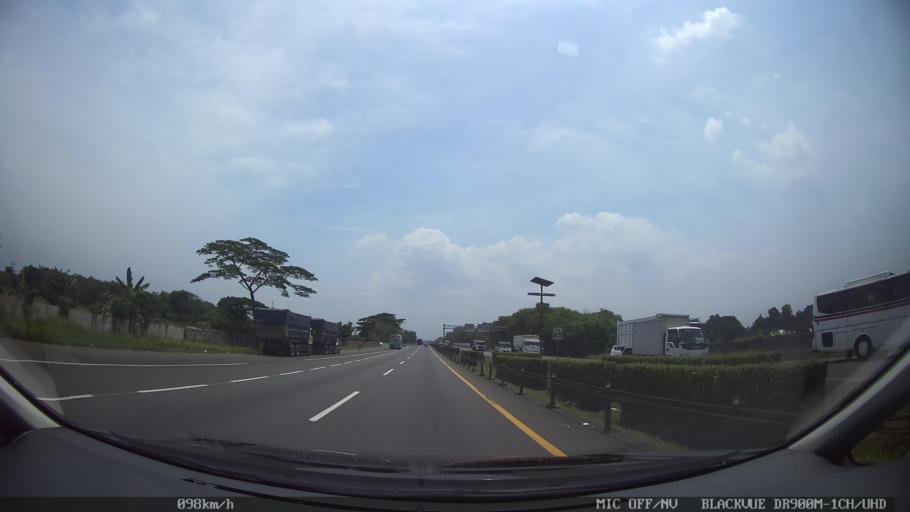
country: ID
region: Banten
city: Serang
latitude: -6.1386
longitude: 106.2387
